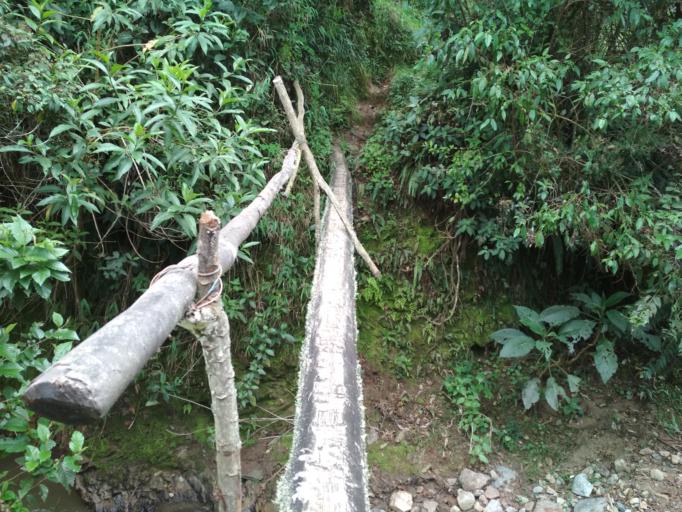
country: CO
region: Cauca
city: Jambalo
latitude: 2.7385
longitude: -76.3457
